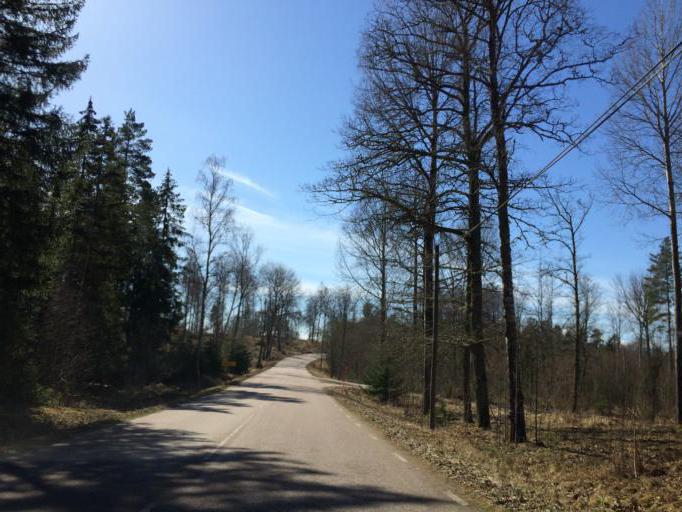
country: SE
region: Soedermanland
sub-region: Eskilstuna Kommun
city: Kvicksund
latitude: 59.5154
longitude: 16.2985
